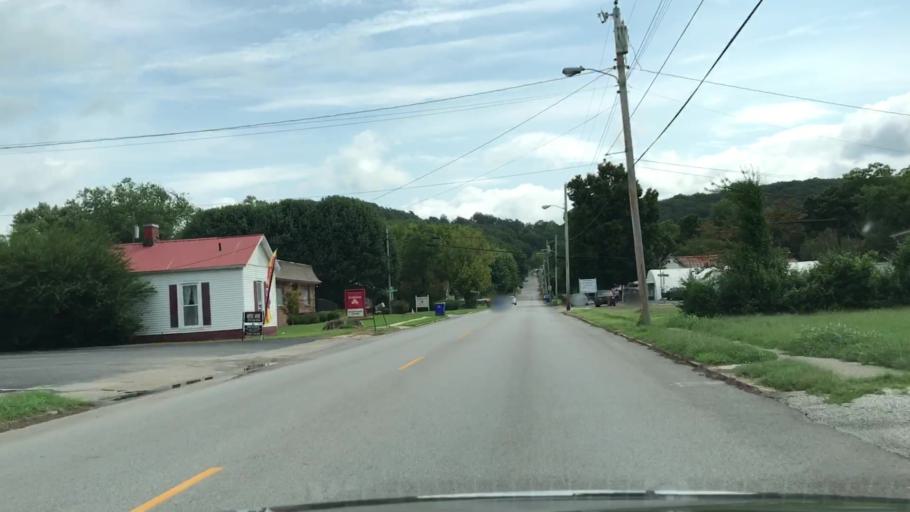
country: US
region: Kentucky
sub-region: Logan County
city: Russellville
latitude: 36.8471
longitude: -86.8807
